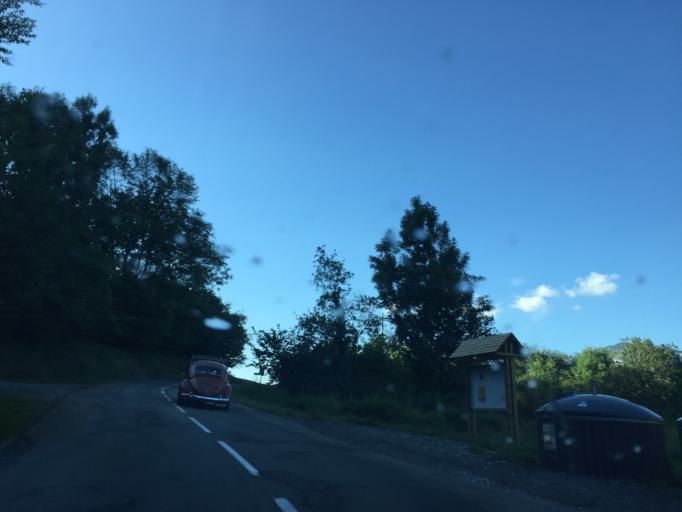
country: FR
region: Rhone-Alpes
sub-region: Departement de la Savoie
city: Challes-les-Eaux
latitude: 45.5533
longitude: 6.0304
